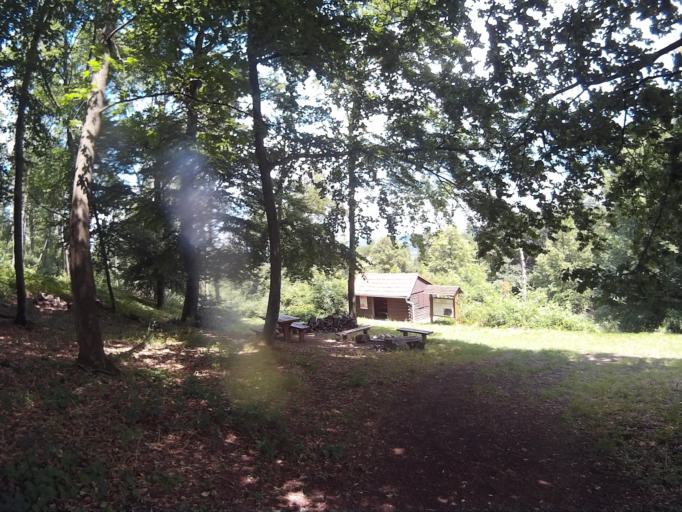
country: HU
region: Veszprem
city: Herend
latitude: 47.1080
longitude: 17.7887
